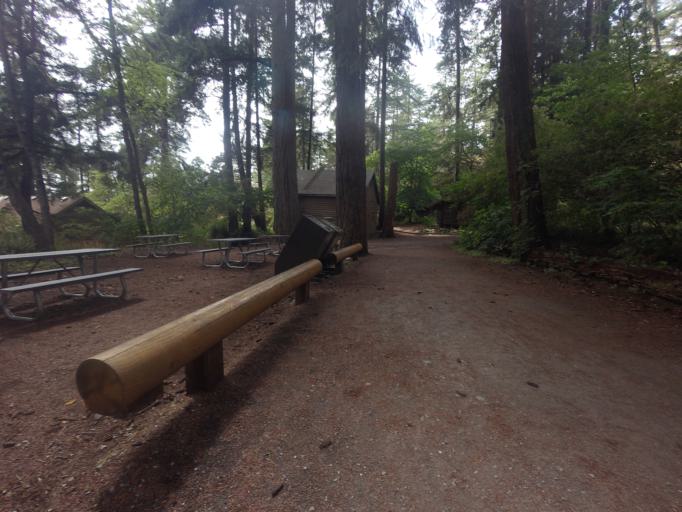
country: CA
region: British Columbia
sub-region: Greater Vancouver Regional District
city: Bowen Island
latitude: 49.3318
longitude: -123.2635
